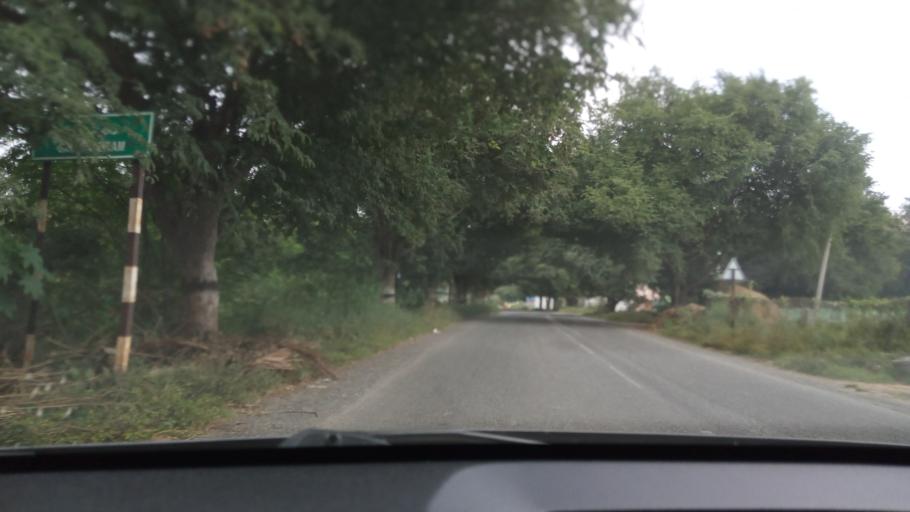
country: IN
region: Andhra Pradesh
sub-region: Chittoor
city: Madanapalle
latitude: 13.6518
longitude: 78.8159
